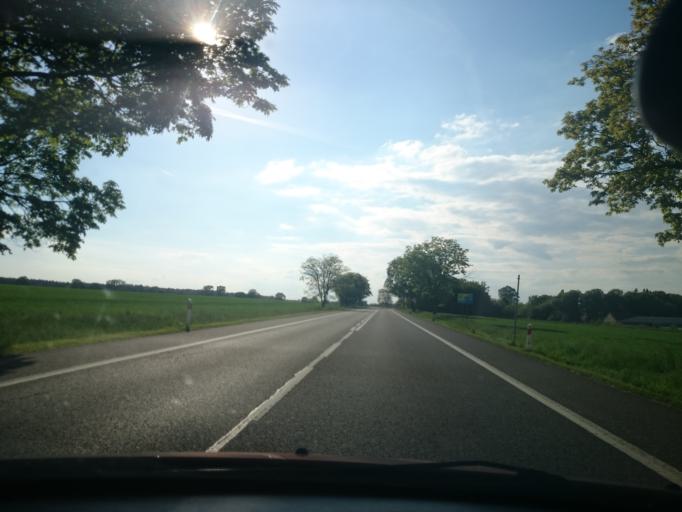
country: PL
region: Silesian Voivodeship
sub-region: Powiat gliwicki
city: Toszek
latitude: 50.4677
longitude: 18.4783
